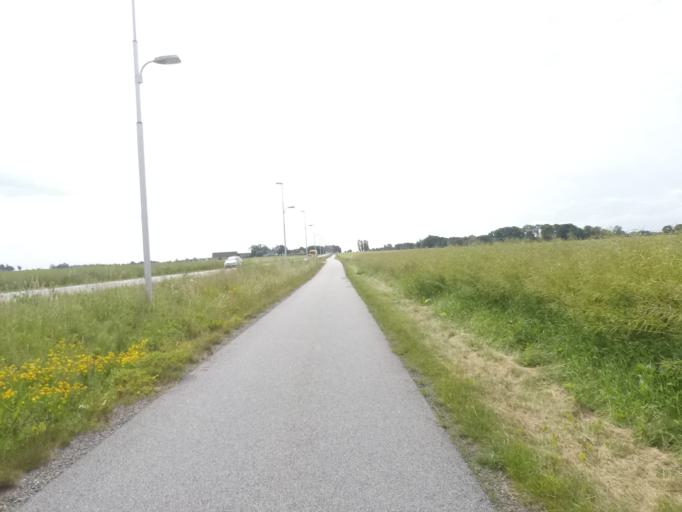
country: SE
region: Skane
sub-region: Malmo
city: Tygelsjo
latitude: 55.5352
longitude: 12.9882
